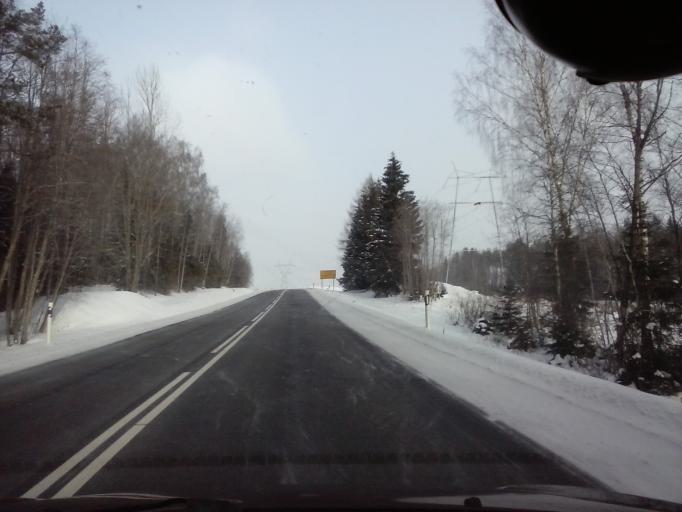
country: EE
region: Viljandimaa
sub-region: Abja vald
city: Abja-Paluoja
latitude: 58.2712
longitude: 25.2665
